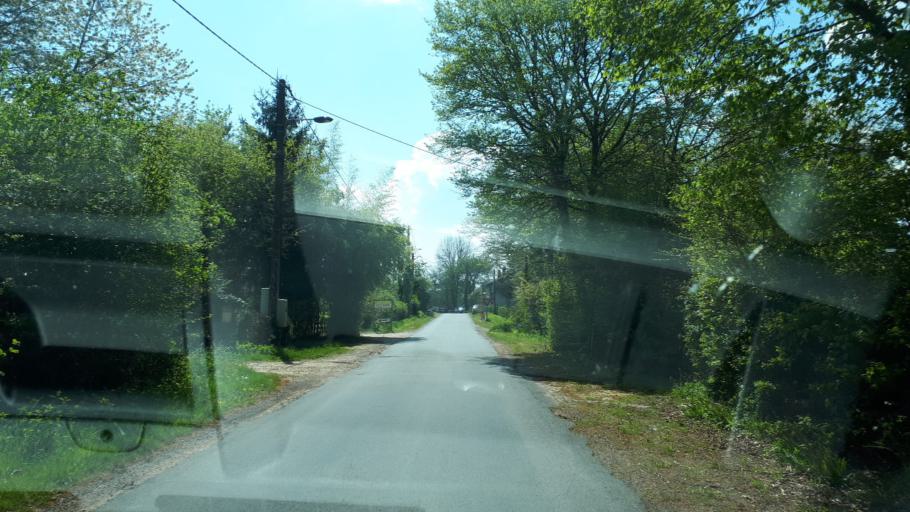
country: FR
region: Centre
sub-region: Departement du Cher
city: Henrichemont
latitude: 47.2869
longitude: 2.5763
